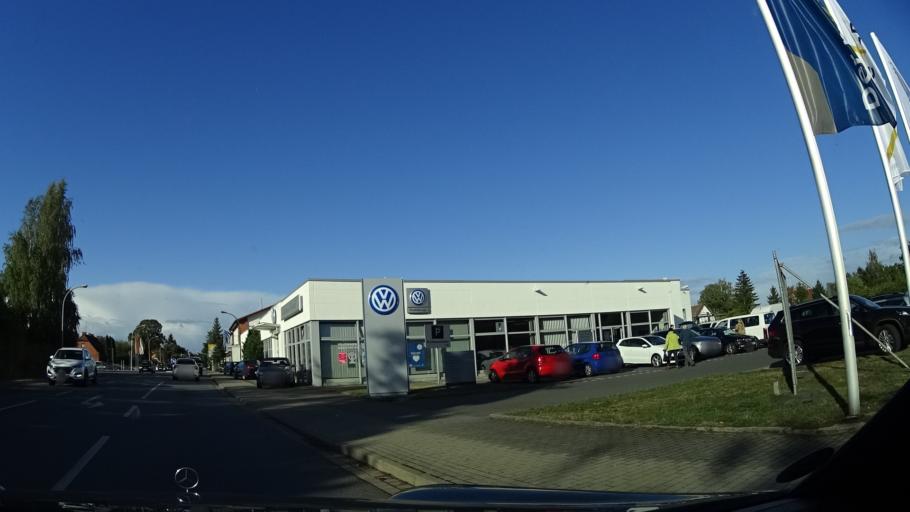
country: DE
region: Brandenburg
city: Neuruppin
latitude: 52.8913
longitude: 12.7980
